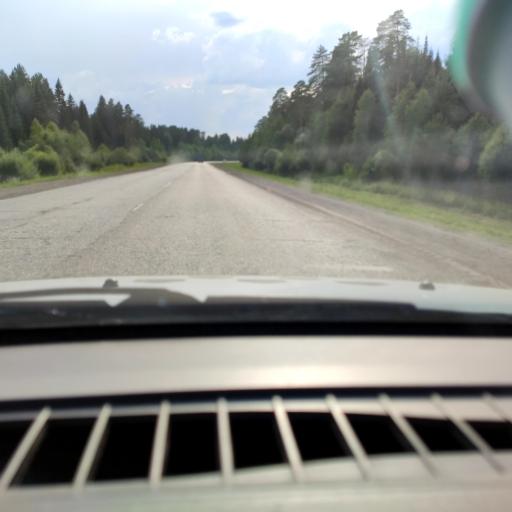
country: RU
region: Udmurtiya
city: Debesy
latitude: 57.6330
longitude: 53.7897
